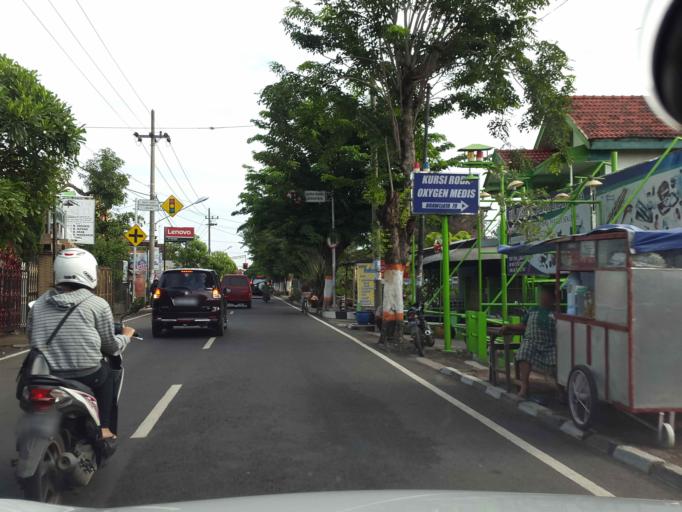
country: ID
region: East Java
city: Mojokerto
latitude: -7.4679
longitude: 112.4298
